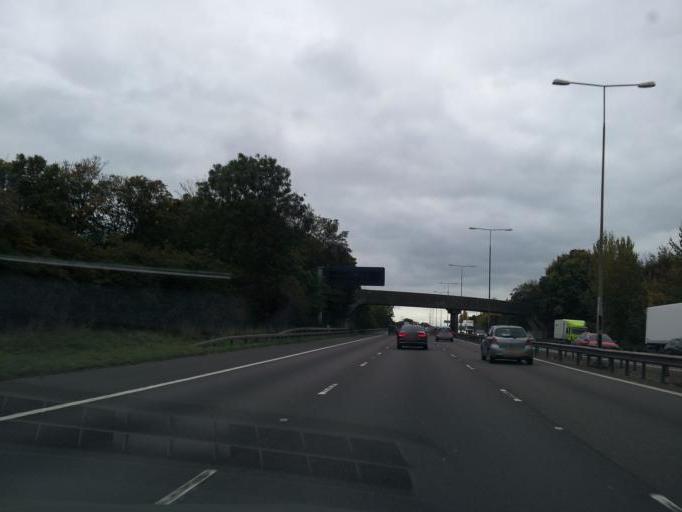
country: GB
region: England
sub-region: Northamptonshire
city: Roade
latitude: 52.1748
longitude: -0.8751
